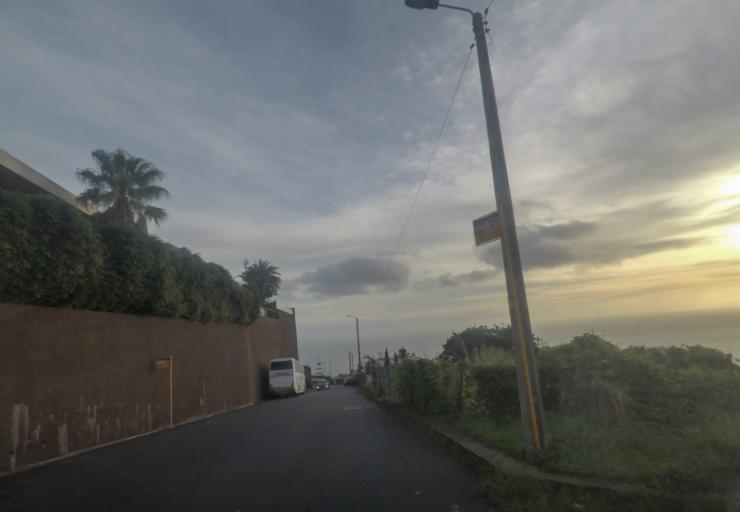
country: PT
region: Madeira
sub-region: Funchal
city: Nossa Senhora do Monte
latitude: 32.6549
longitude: -16.8770
